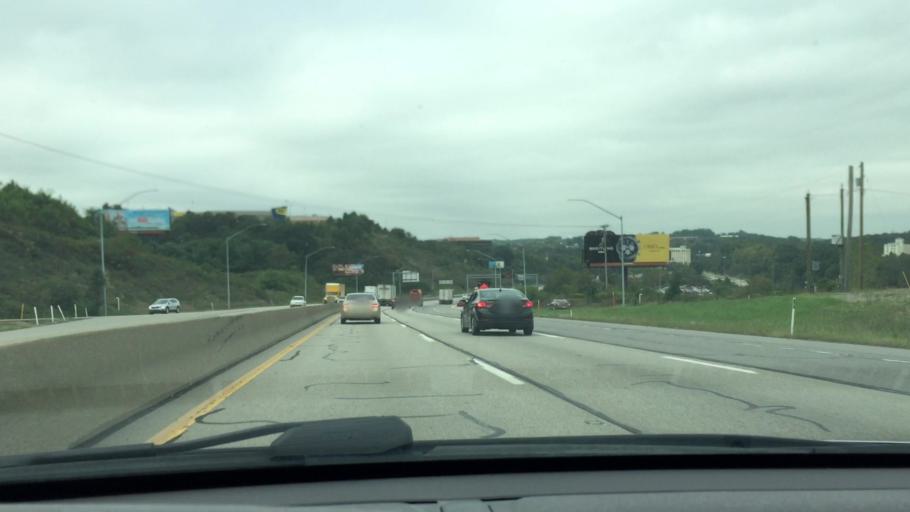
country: US
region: Pennsylvania
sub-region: Allegheny County
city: Oakdale
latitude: 40.4524
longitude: -80.1750
